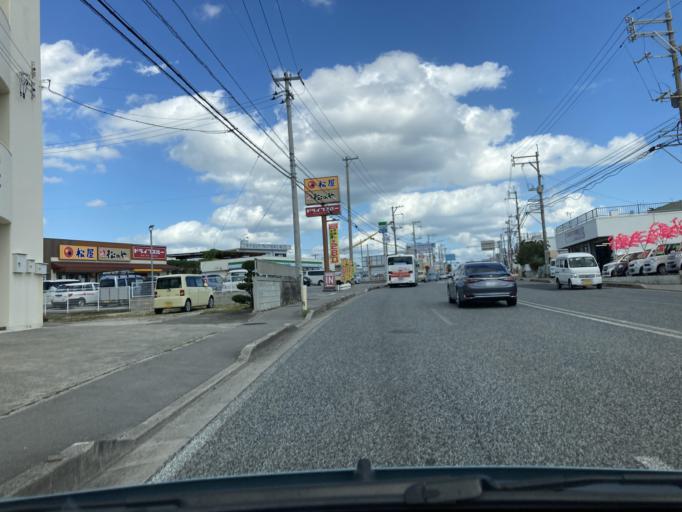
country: JP
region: Okinawa
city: Okinawa
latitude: 26.3658
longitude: 127.8154
